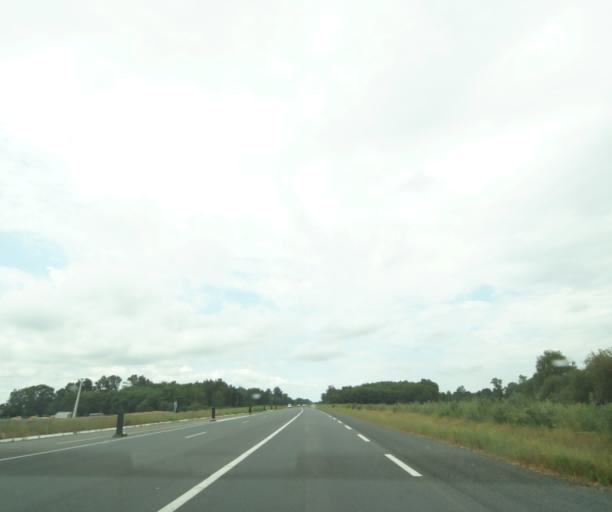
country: FR
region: Poitou-Charentes
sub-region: Departement des Deux-Sevres
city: Louzy
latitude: 47.0709
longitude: -0.1782
